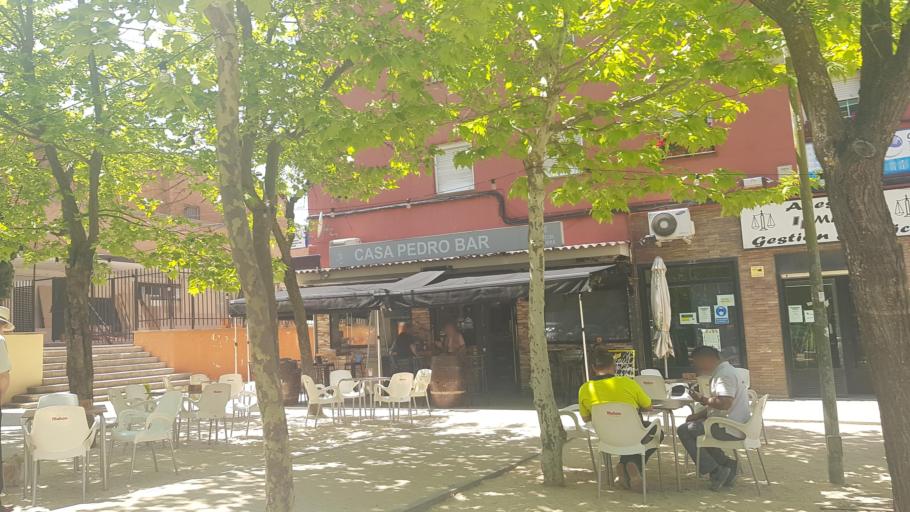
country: ES
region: Madrid
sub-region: Provincia de Madrid
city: Villaverde
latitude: 40.3599
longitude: -3.6963
